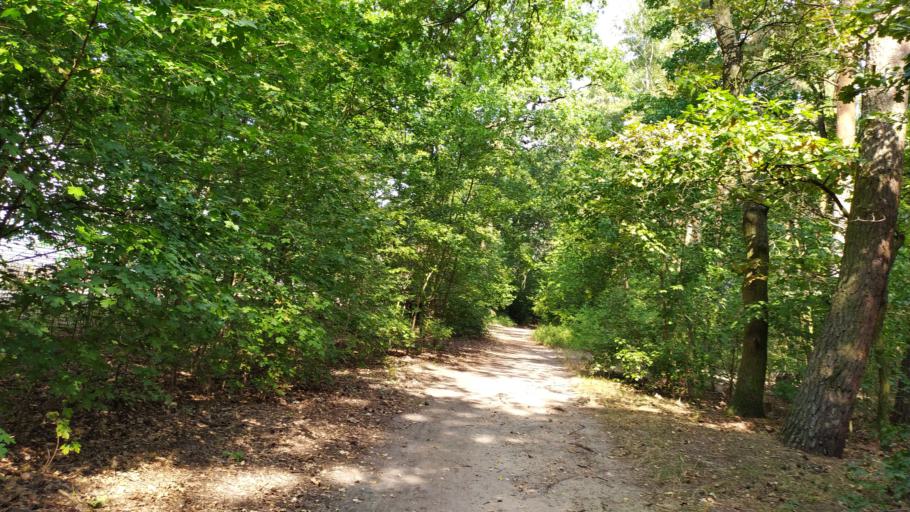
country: DE
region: Berlin
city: Grunau
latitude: 52.4274
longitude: 13.5970
